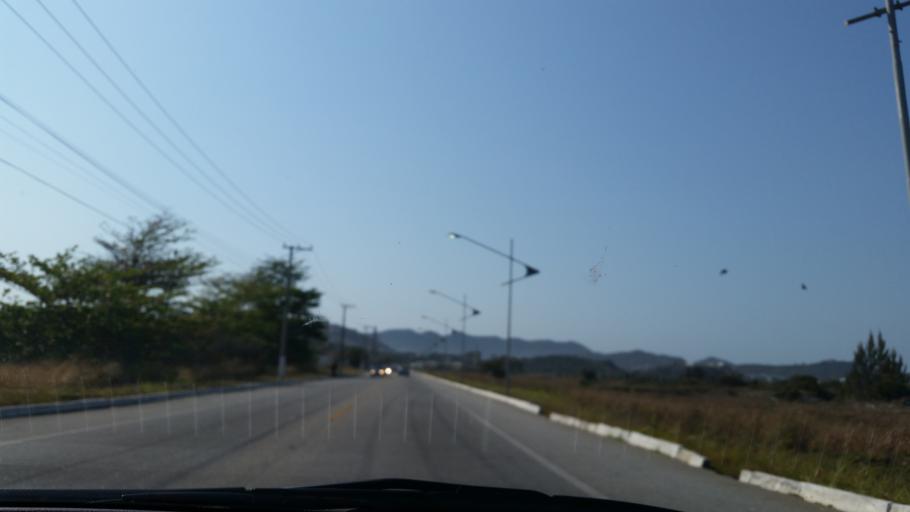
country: BR
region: Rio de Janeiro
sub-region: Arraial Do Cabo
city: Arraial do Cabo
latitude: -22.9534
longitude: -42.0411
